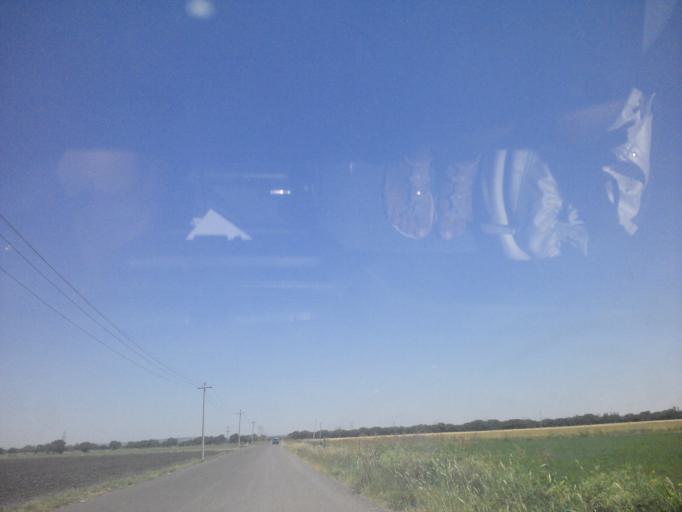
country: MX
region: Guanajuato
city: San Roque
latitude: 20.9550
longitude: -101.8948
